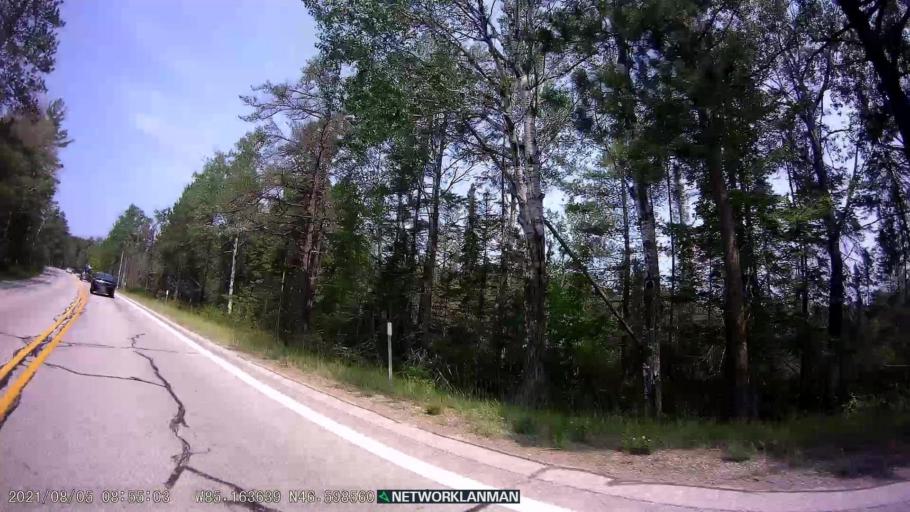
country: US
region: Michigan
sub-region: Luce County
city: Newberry
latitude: 46.5986
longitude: -85.1638
